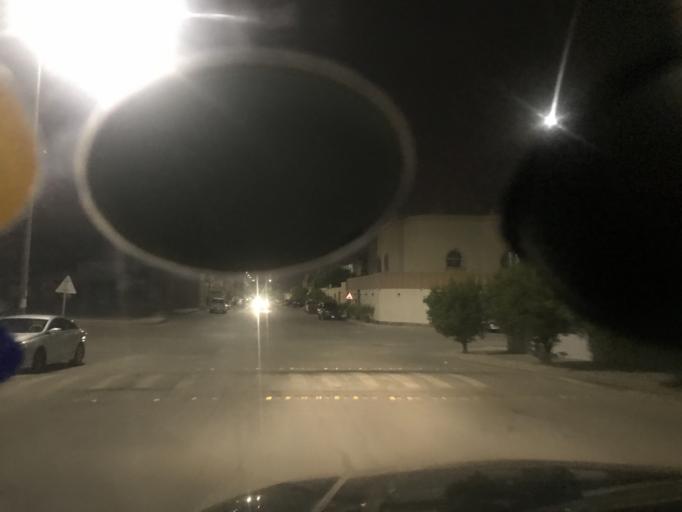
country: SA
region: Ar Riyad
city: Riyadh
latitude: 24.7355
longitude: 46.7680
